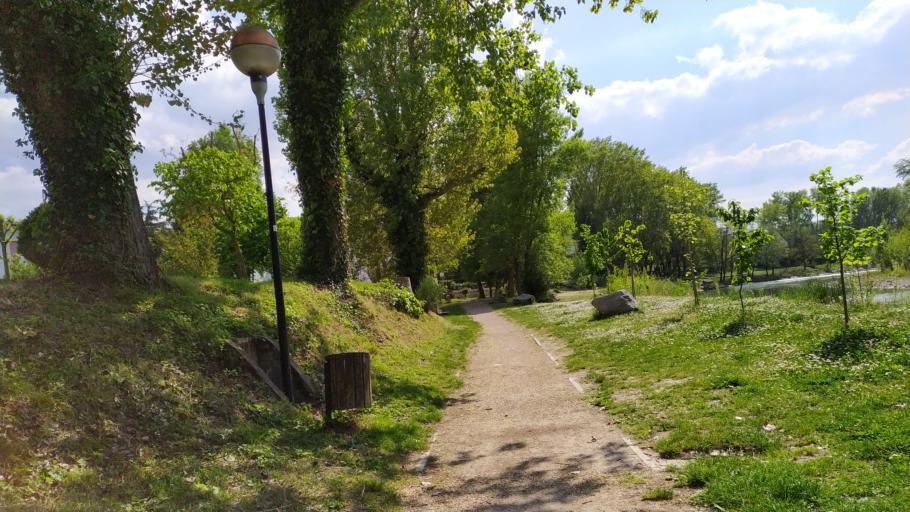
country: IT
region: Emilia-Romagna
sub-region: Provincia di Bologna
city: Borgo Tossignano
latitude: 44.2772
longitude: 11.5860
